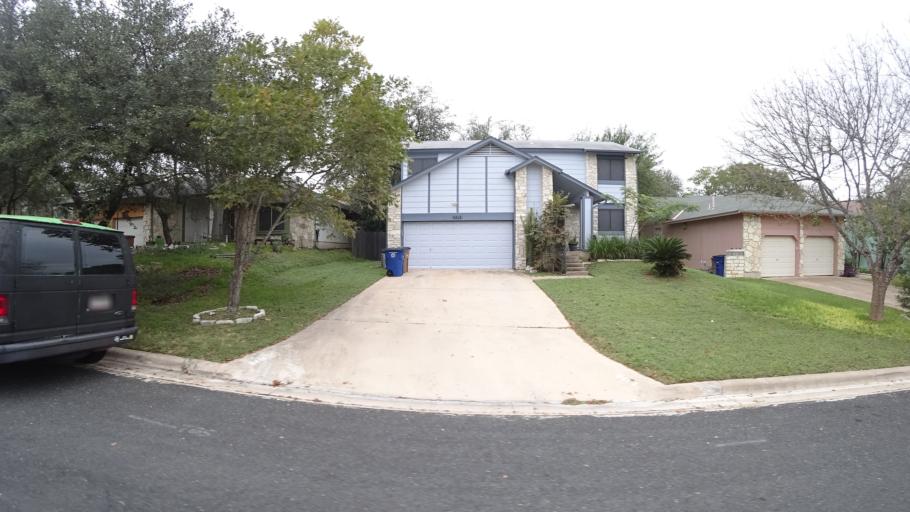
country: US
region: Texas
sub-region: Travis County
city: Barton Creek
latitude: 30.2403
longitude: -97.8964
